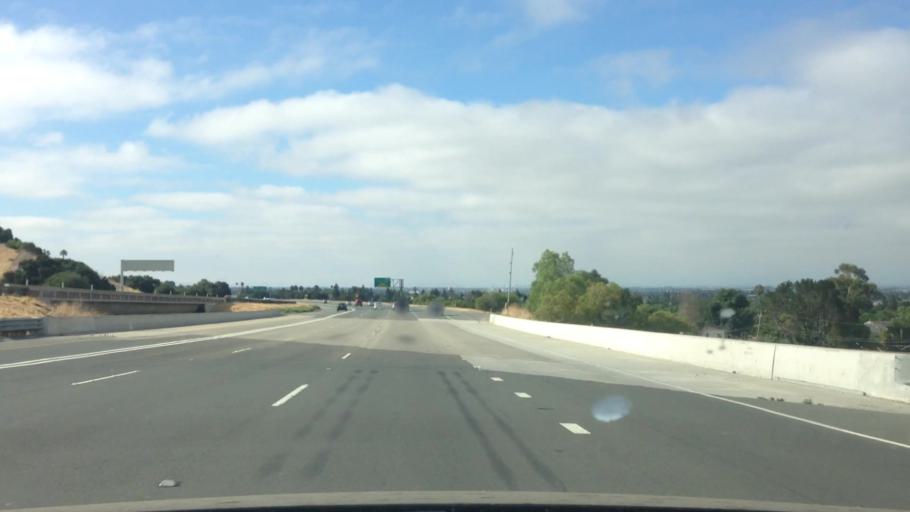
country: US
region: California
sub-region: Santa Clara County
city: Milpitas
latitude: 37.4757
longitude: -121.9116
